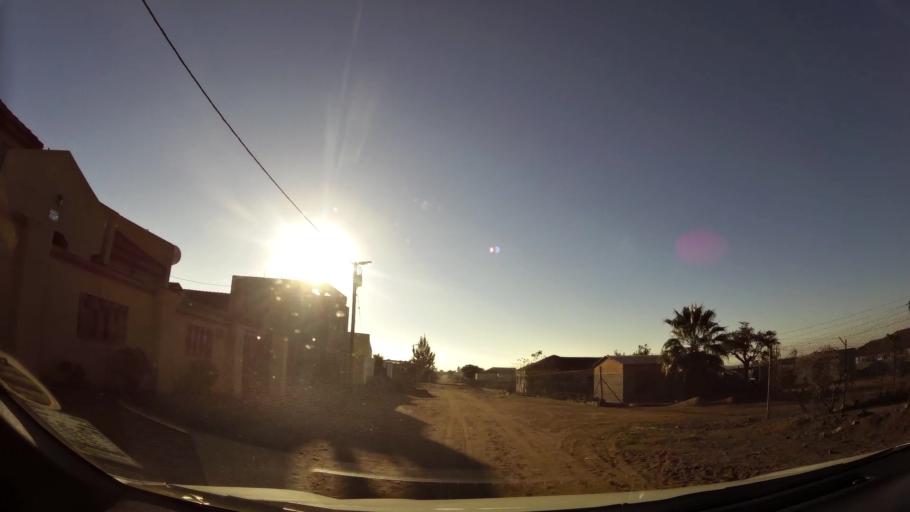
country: ZA
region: Limpopo
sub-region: Capricorn District Municipality
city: Polokwane
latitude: -23.8397
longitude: 29.3547
